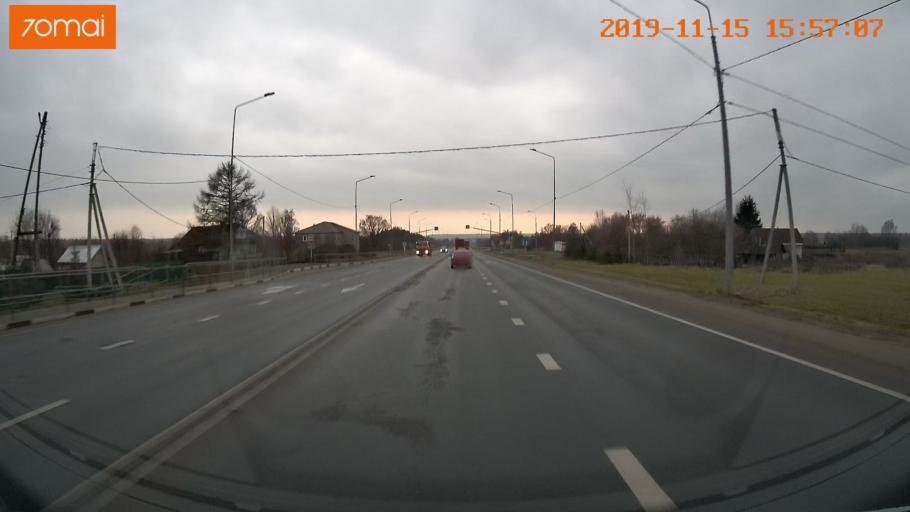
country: RU
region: Jaroslavl
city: Yaroslavl
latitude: 57.8340
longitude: 39.9666
